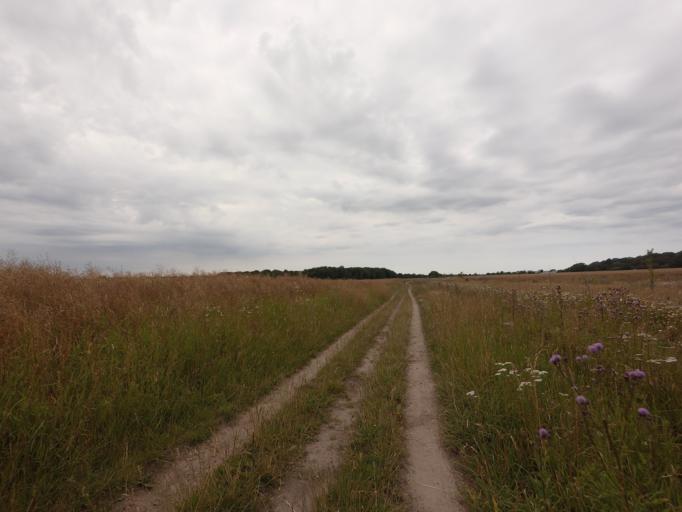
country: SE
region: Skane
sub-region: Helsingborg
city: Helsingborg
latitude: 56.0889
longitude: 12.6785
